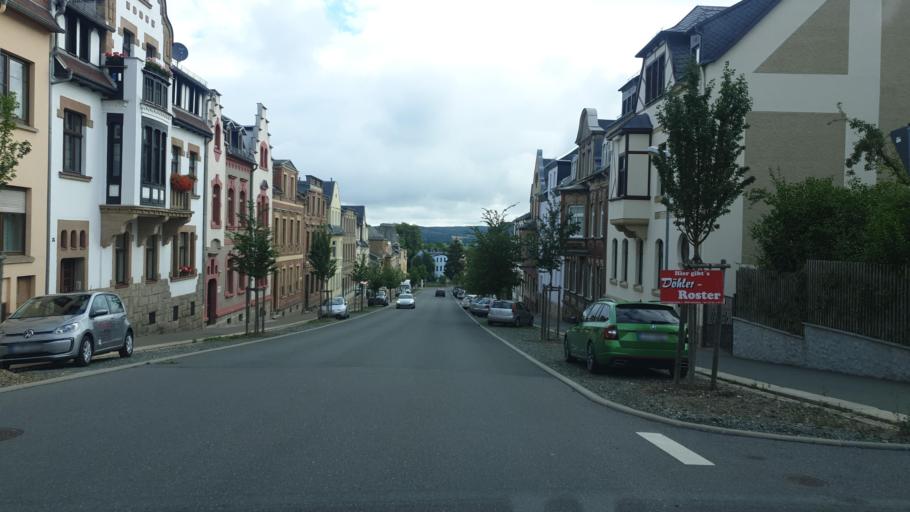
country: DE
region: Saxony
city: Netzschkau
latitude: 50.6077
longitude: 12.2425
